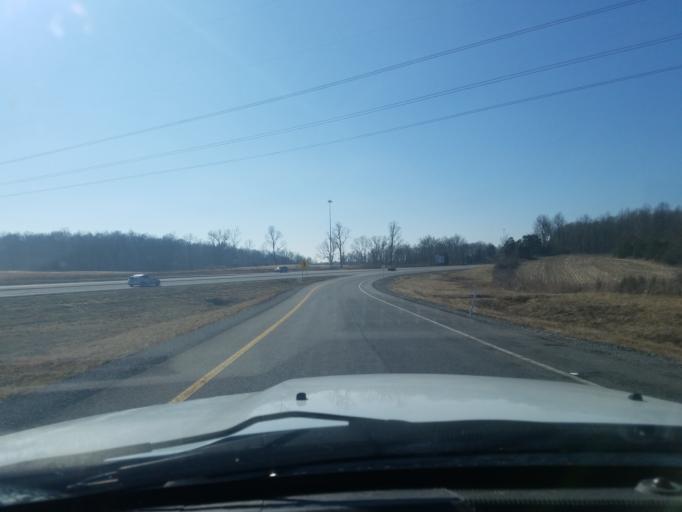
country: US
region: Kentucky
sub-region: Hardin County
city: Elizabethtown
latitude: 37.6535
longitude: -85.8920
